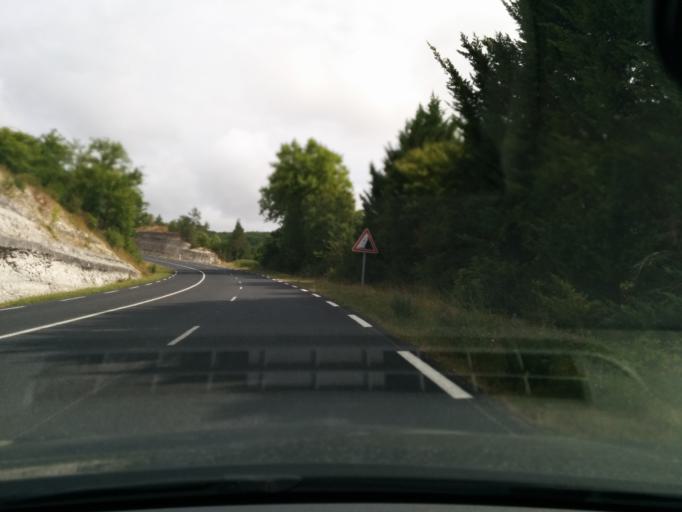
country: FR
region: Midi-Pyrenees
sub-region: Departement du Lot
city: Le Vigan
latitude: 44.7088
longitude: 1.4837
